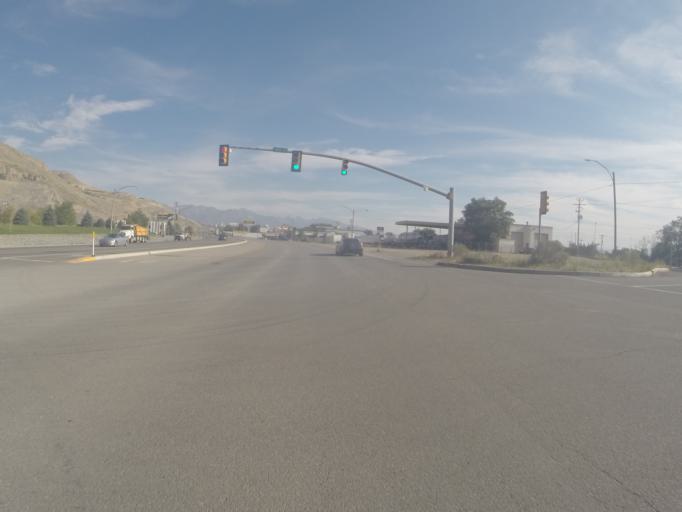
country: US
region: Utah
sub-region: Davis County
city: North Salt Lake
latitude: 40.8062
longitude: -111.9179
